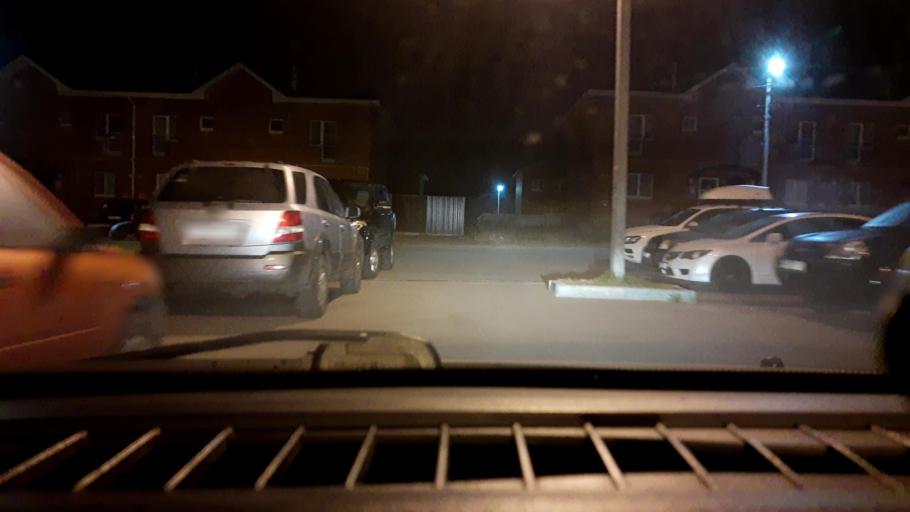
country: RU
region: Nizjnij Novgorod
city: Afonino
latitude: 56.2121
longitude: 44.0905
